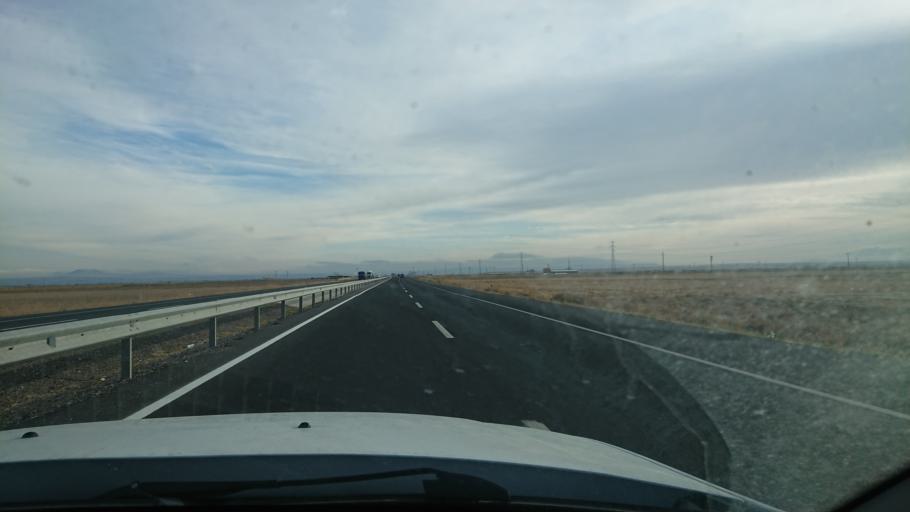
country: TR
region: Aksaray
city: Yesilova
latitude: 38.3078
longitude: 33.8214
